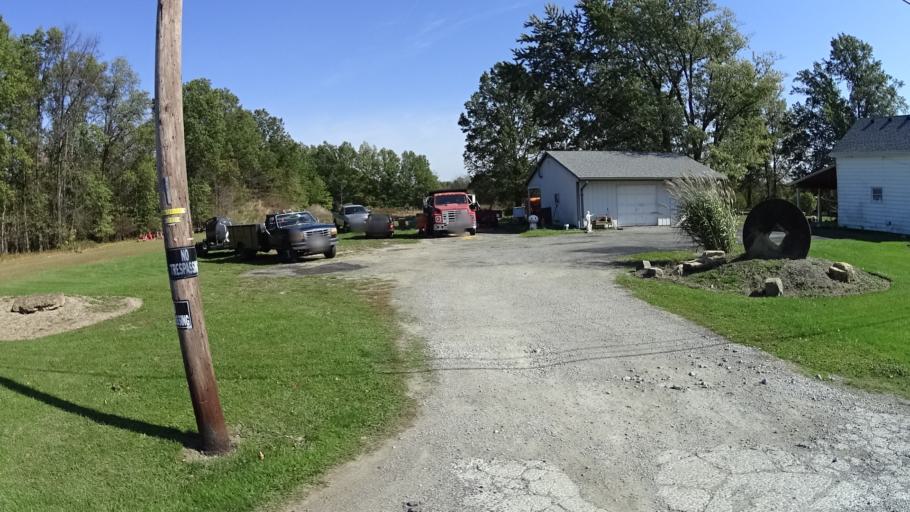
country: US
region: Ohio
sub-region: Lorain County
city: Vermilion-on-the-Lake
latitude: 41.4148
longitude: -82.3044
